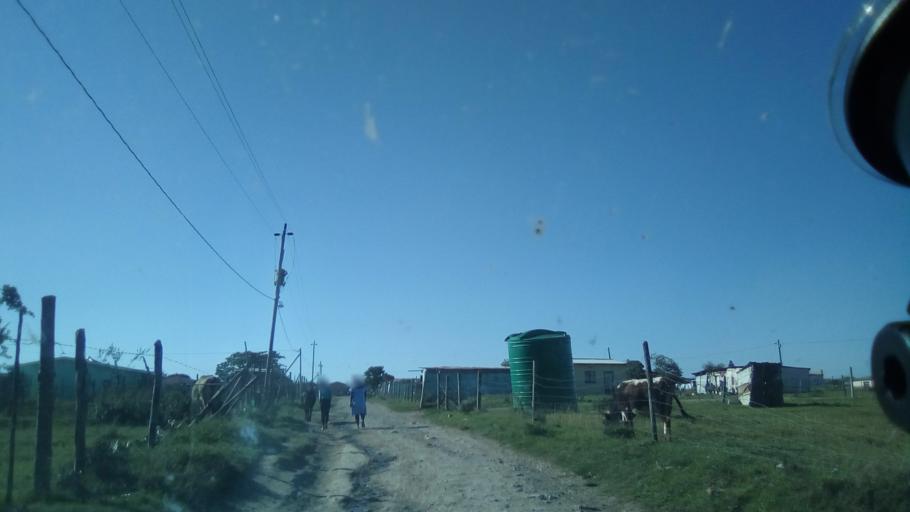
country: ZA
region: Eastern Cape
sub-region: Buffalo City Metropolitan Municipality
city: Bhisho
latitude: -32.8275
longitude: 27.3701
